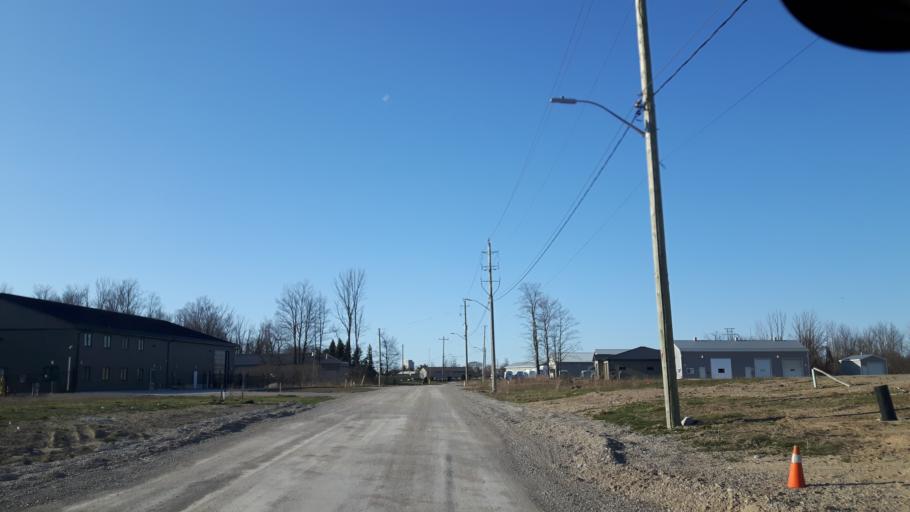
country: CA
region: Ontario
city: Goderich
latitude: 43.7267
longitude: -81.6935
